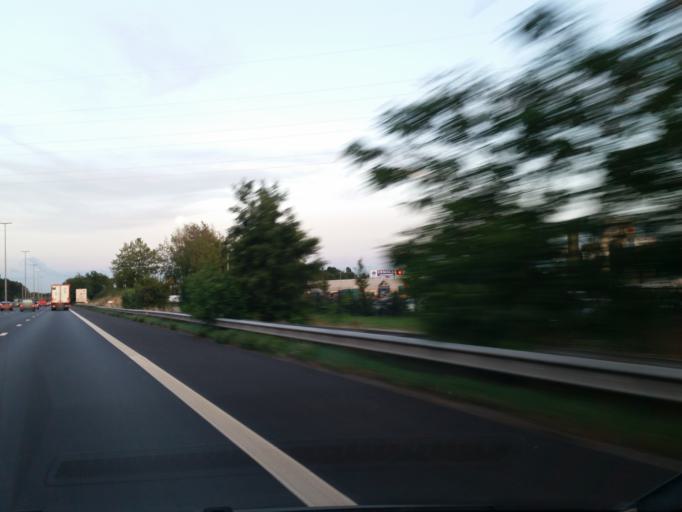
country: BE
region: Flanders
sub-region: Provincie Oost-Vlaanderen
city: Sint-Martens-Latem
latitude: 51.0436
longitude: 3.6012
